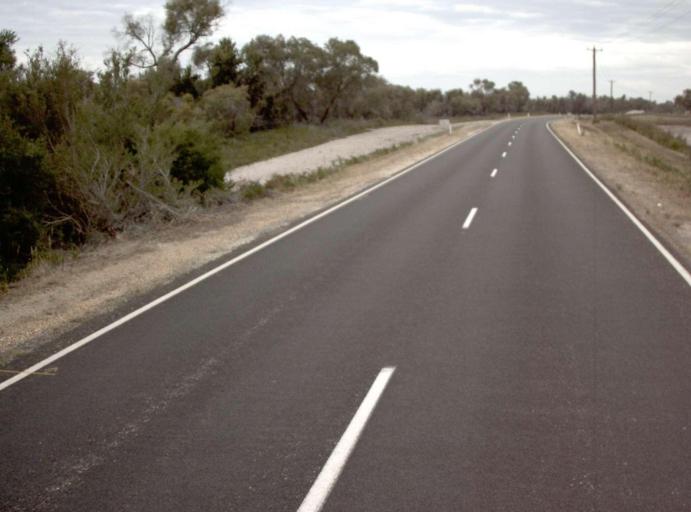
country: AU
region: Victoria
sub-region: Wellington
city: Sale
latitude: -38.1617
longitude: 147.3901
